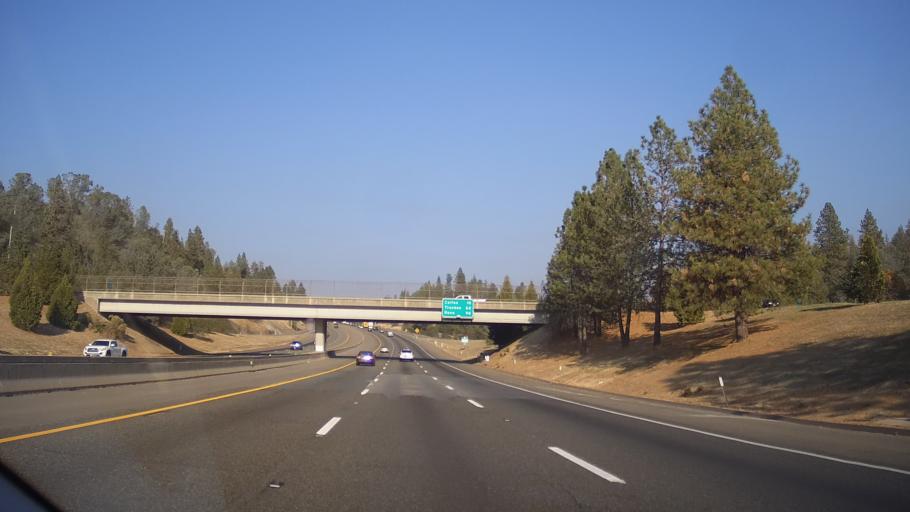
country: US
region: California
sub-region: Placer County
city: Meadow Vista
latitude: 38.9689
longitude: -121.0184
